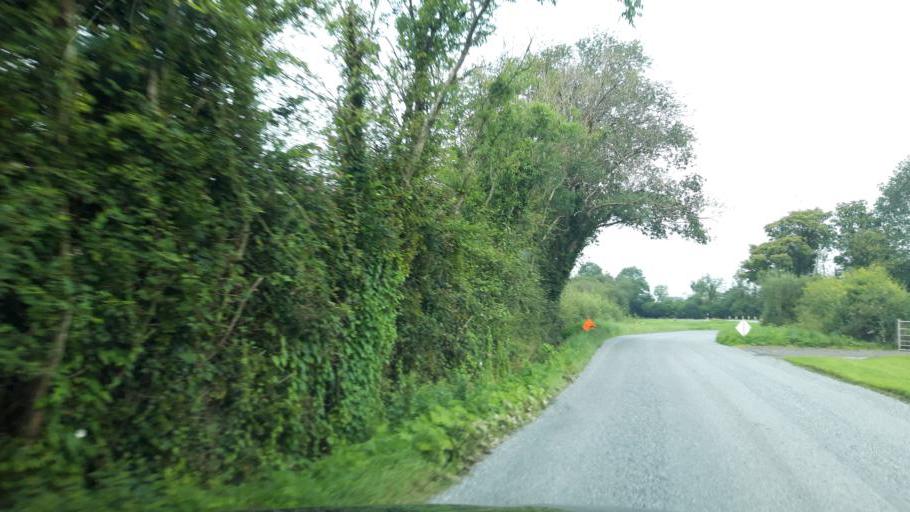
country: IE
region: Leinster
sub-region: Kilkenny
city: Callan
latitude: 52.5229
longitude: -7.5104
